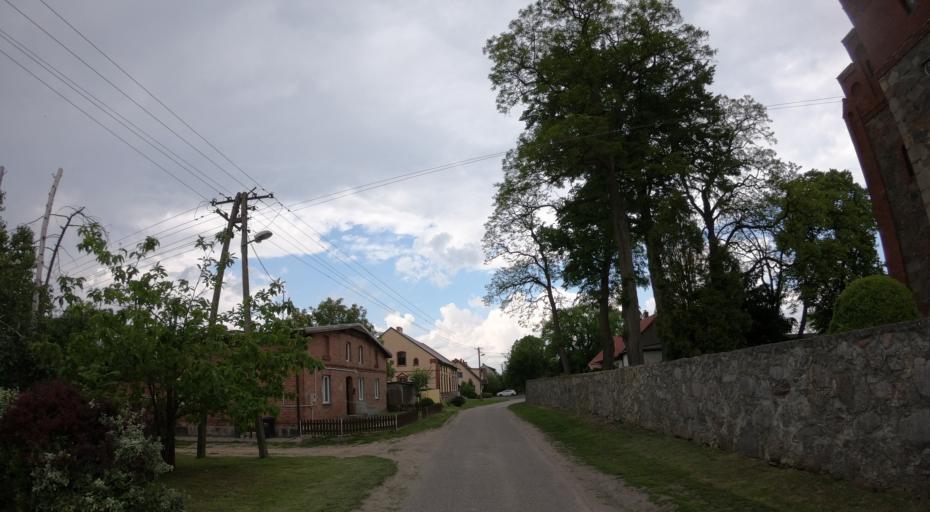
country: PL
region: West Pomeranian Voivodeship
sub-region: Powiat pyrzycki
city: Bielice
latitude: 53.2294
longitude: 14.7657
